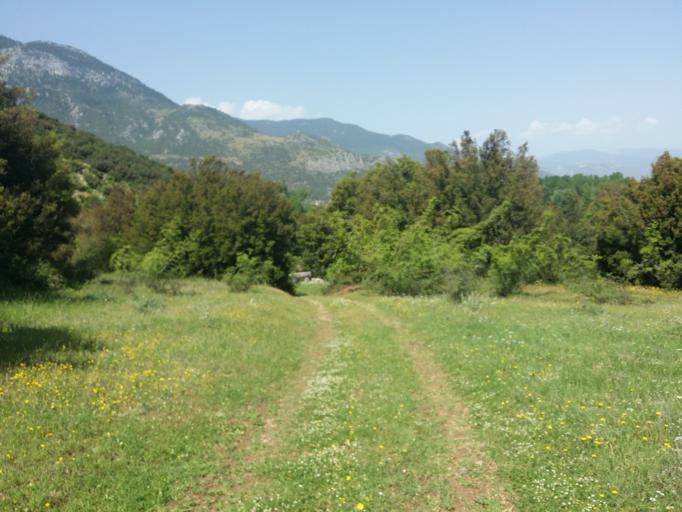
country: GR
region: Central Greece
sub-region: Nomos Fthiotidos
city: Amfikleia
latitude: 38.6290
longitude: 22.5222
